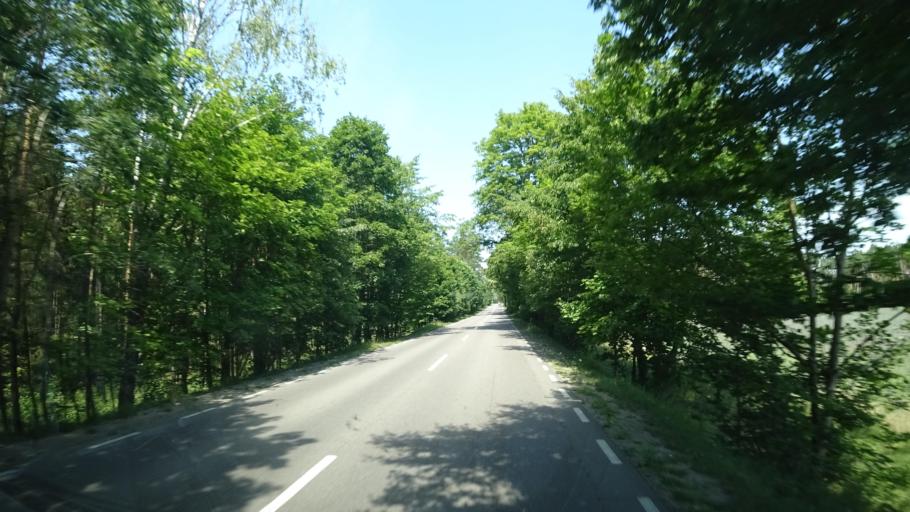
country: PL
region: Pomeranian Voivodeship
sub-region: Powiat koscierski
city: Dziemiany
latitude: 53.9921
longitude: 17.7681
